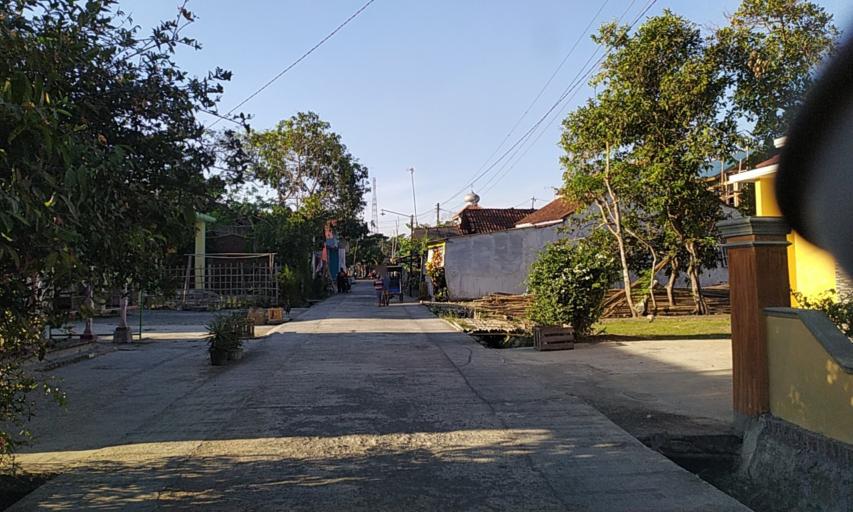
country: ID
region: Central Java
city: Sidareja
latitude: -7.4907
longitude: 108.7944
